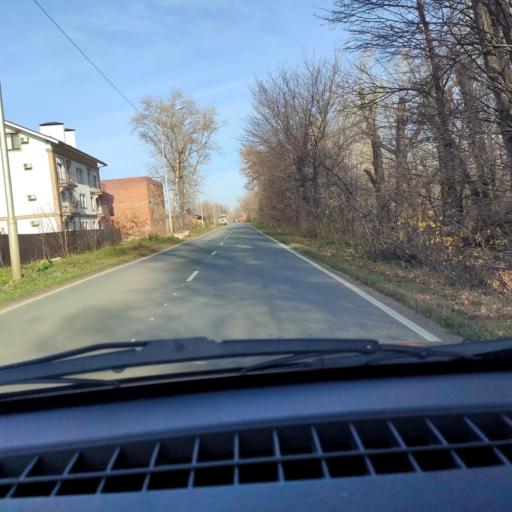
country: RU
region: Bashkortostan
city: Ufa
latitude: 54.6645
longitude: 55.9386
